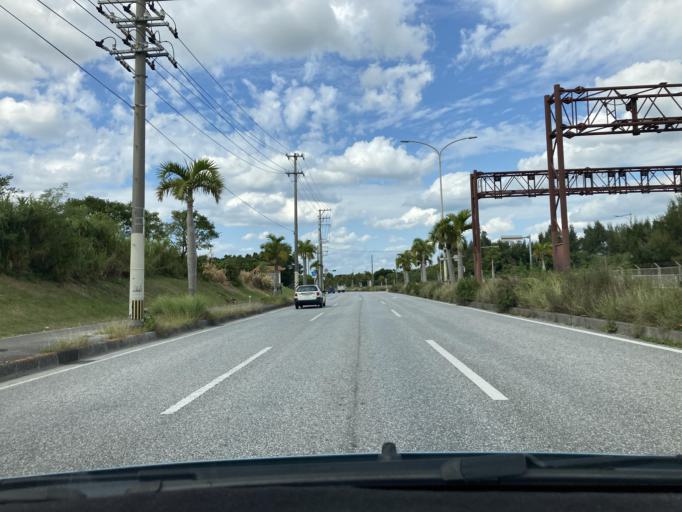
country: JP
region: Okinawa
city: Chatan
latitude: 26.3492
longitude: 127.7468
